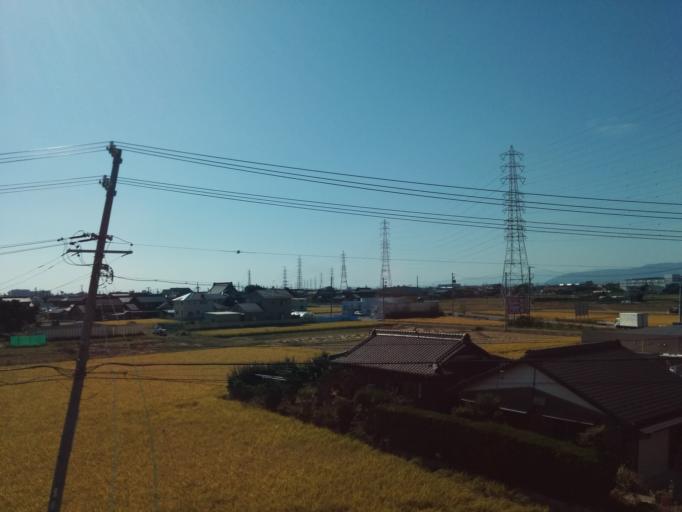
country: JP
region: Aichi
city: Inazawa
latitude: 35.2308
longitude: 136.7986
